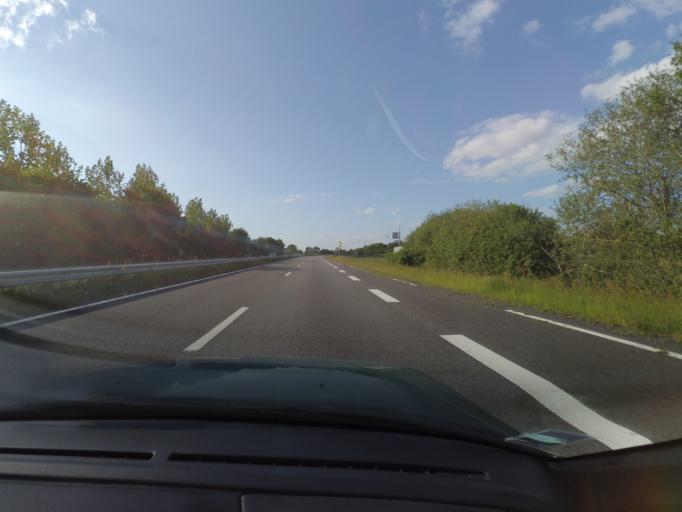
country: FR
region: Pays de la Loire
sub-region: Departement de la Vendee
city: Saligny
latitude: 46.8025
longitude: -1.4320
